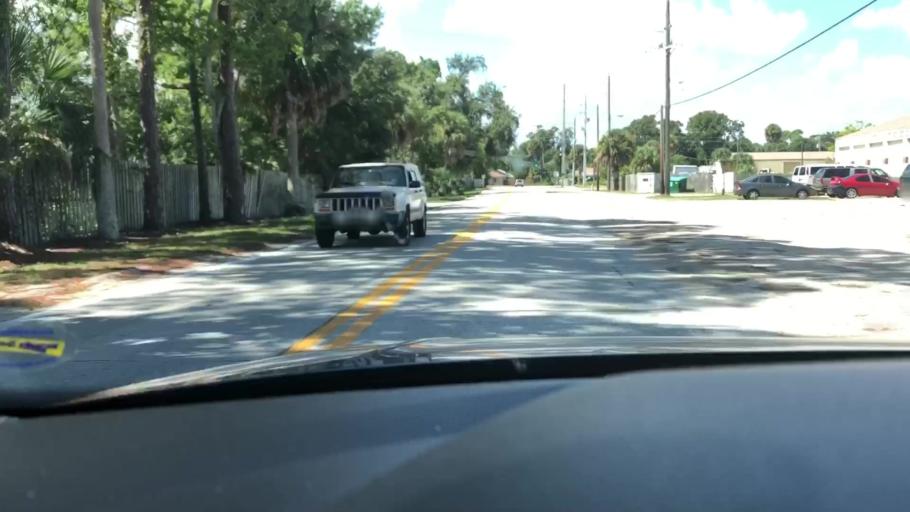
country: US
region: Florida
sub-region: Volusia County
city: Port Orange
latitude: 29.1243
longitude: -80.9909
